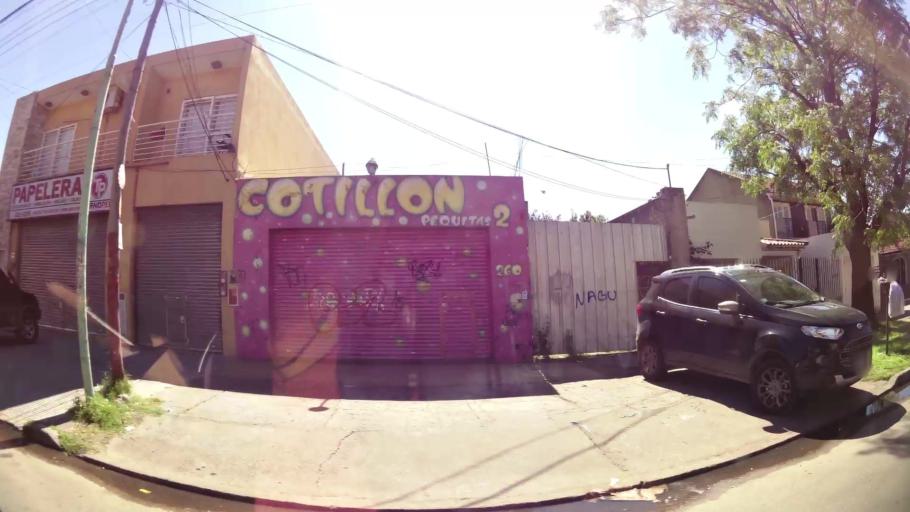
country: AR
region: Buenos Aires
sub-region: Partido de Lomas de Zamora
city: Lomas de Zamora
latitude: -34.7547
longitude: -58.4209
